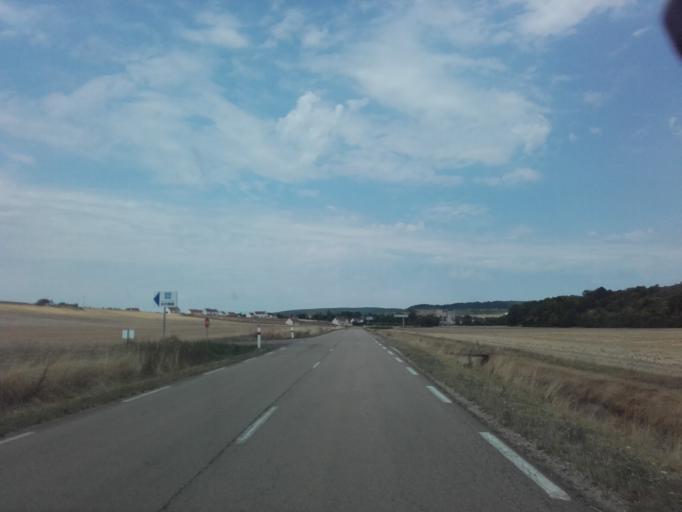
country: FR
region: Bourgogne
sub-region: Departement de l'Yonne
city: Chablis
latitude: 47.7994
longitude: 3.7986
